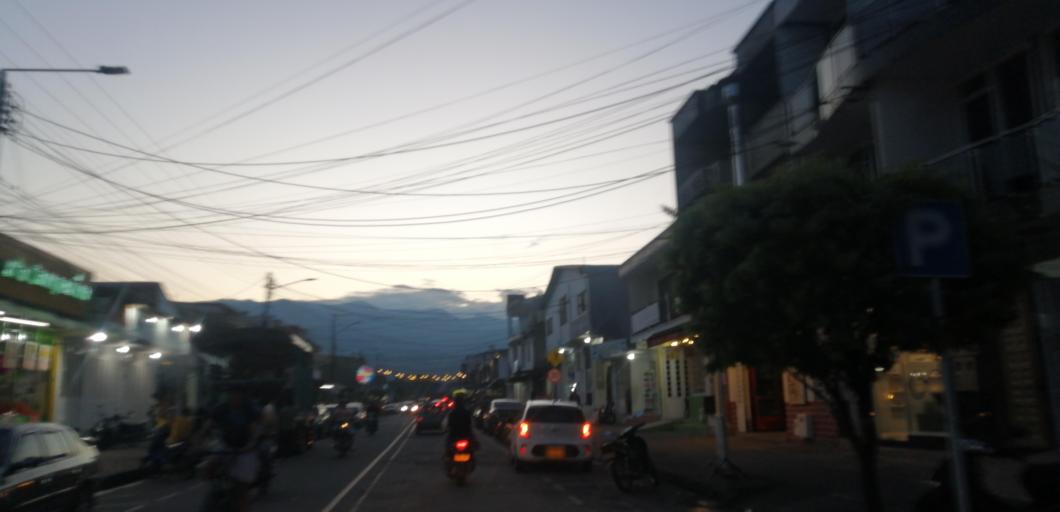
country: CO
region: Meta
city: Acacias
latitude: 3.9881
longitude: -73.7734
